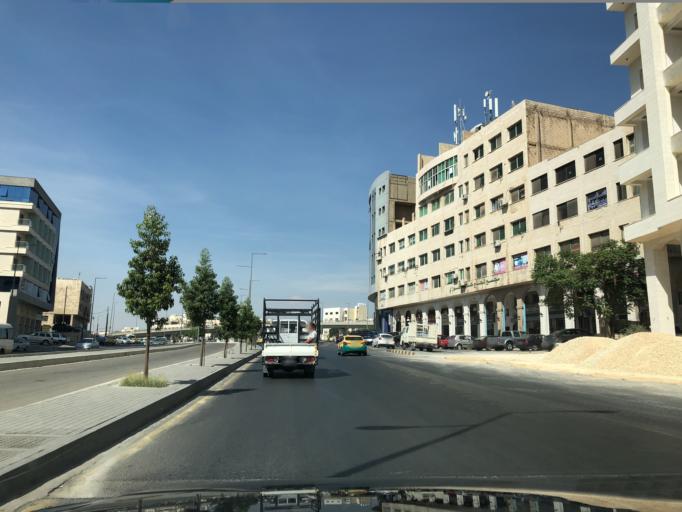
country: JO
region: Amman
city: Al Jubayhah
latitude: 32.0245
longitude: 35.8571
